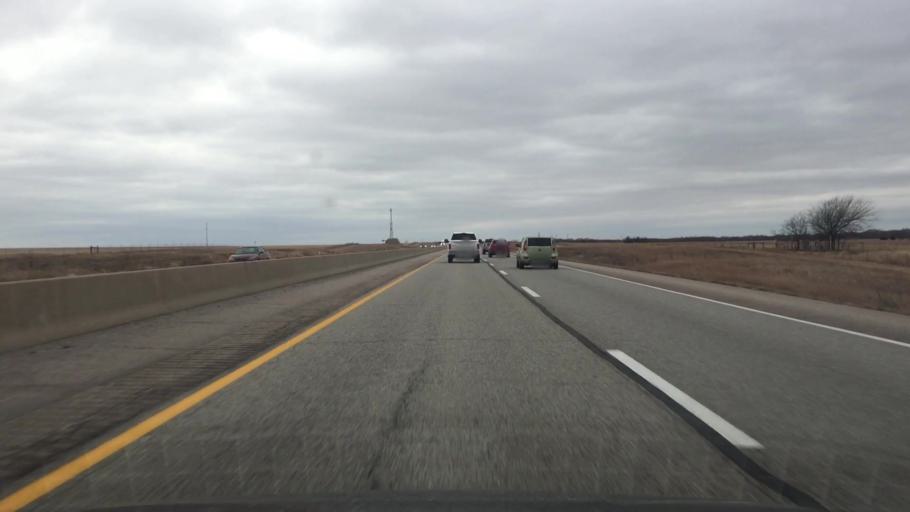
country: US
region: Kansas
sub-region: Butler County
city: El Dorado
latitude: 37.9707
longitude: -96.7219
